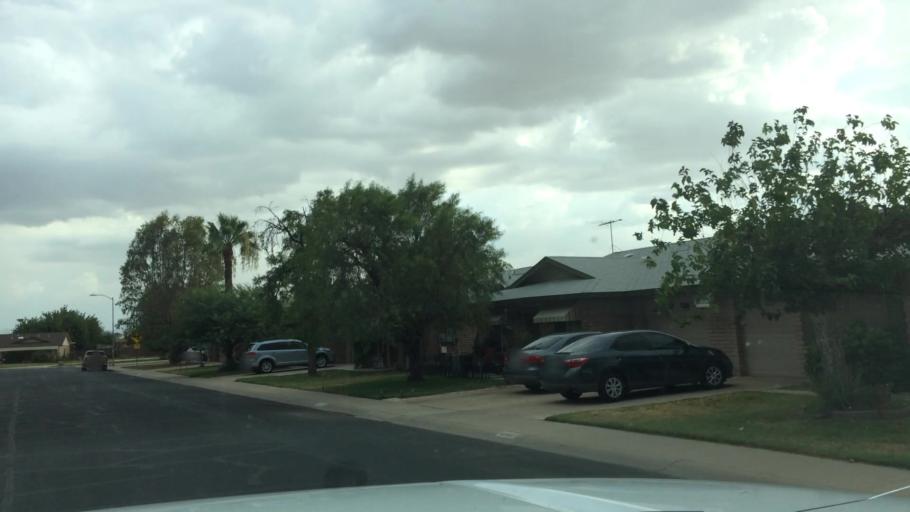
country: US
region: Arizona
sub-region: Maricopa County
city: Sun City
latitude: 33.5748
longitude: -112.2692
